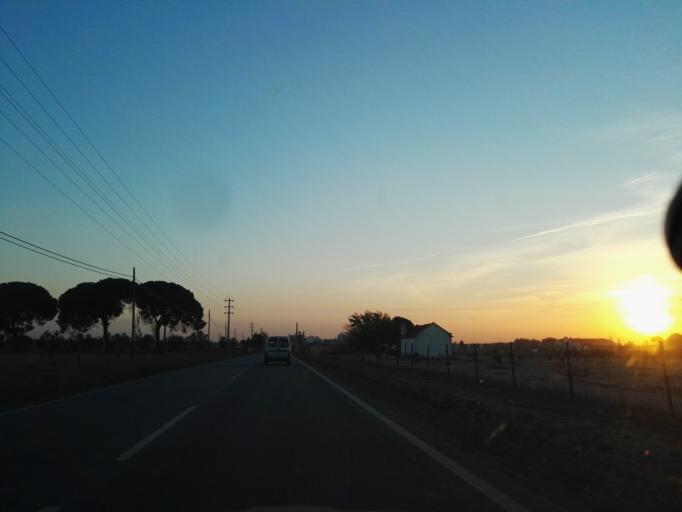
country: PT
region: Santarem
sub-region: Coruche
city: Coruche
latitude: 38.9522
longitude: -8.4951
